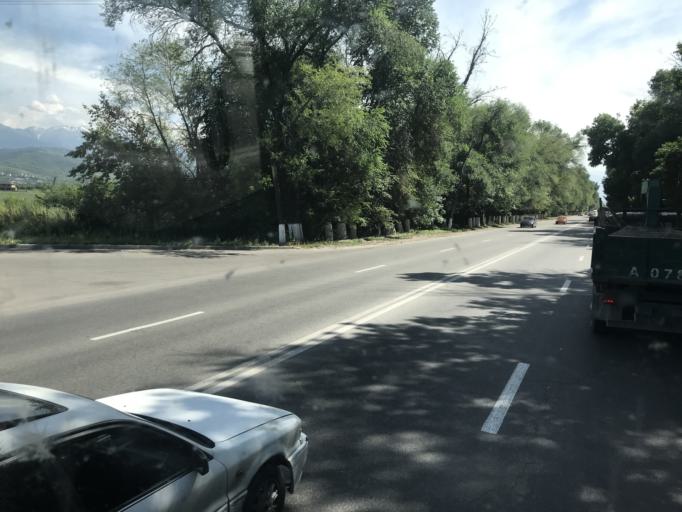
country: KZ
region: Almaty Oblysy
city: Energeticheskiy
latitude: 43.3279
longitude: 77.0324
